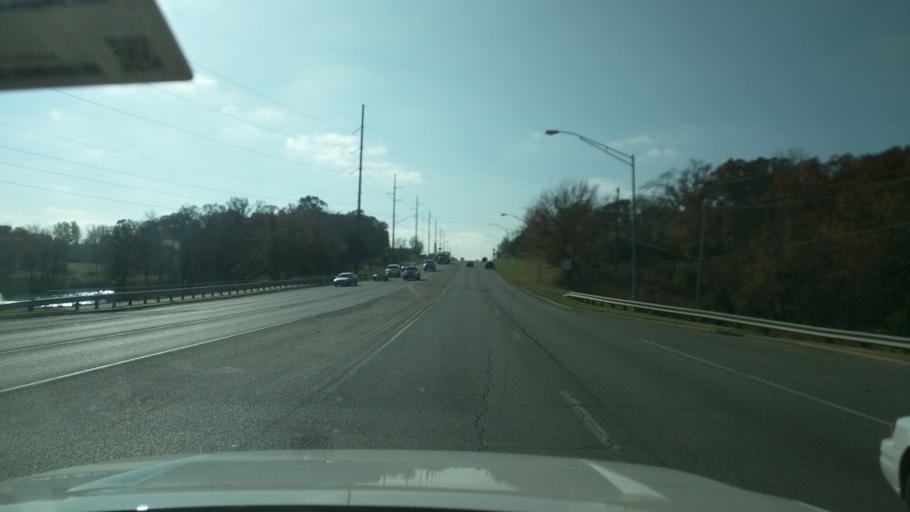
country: US
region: Oklahoma
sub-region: Washington County
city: Bartlesville
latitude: 36.7400
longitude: -95.9354
